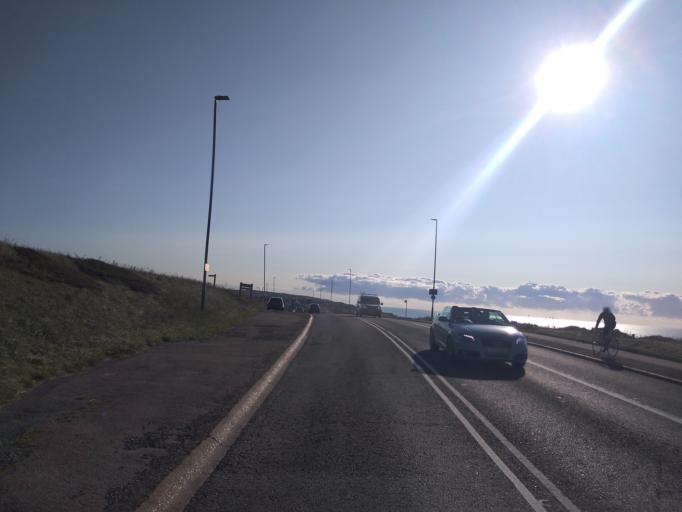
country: GB
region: England
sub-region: East Sussex
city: Peacehaven
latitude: 50.7978
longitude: -0.0300
